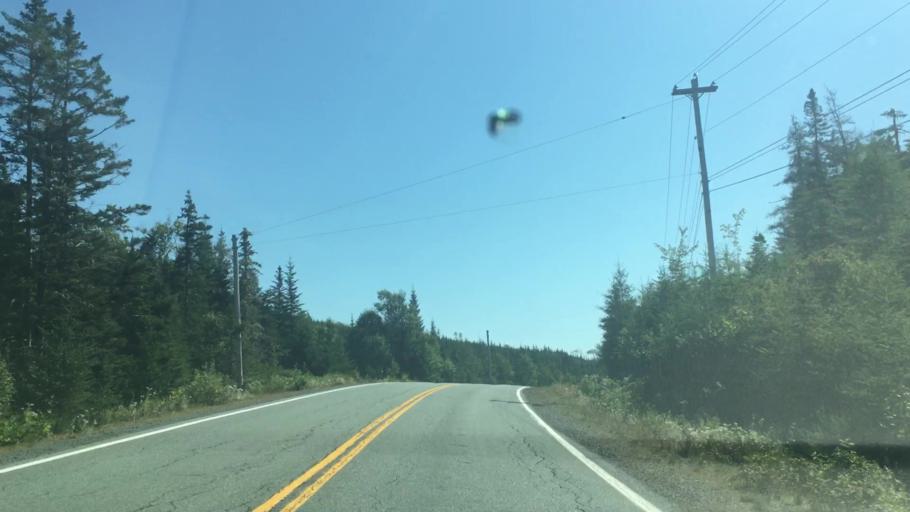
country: CA
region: Nova Scotia
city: Antigonish
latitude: 45.0118
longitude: -62.0926
